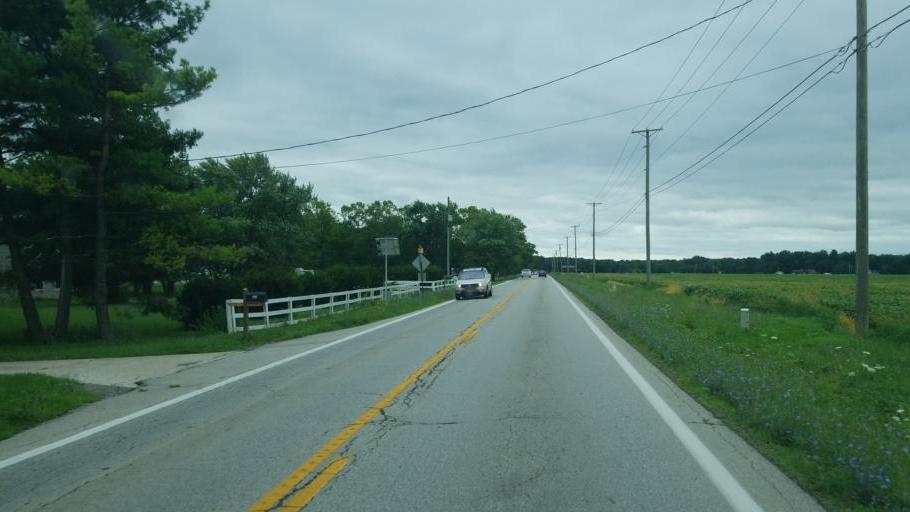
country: US
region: Ohio
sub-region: Pickaway County
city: Commercial Point
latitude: 39.8302
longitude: -83.0184
